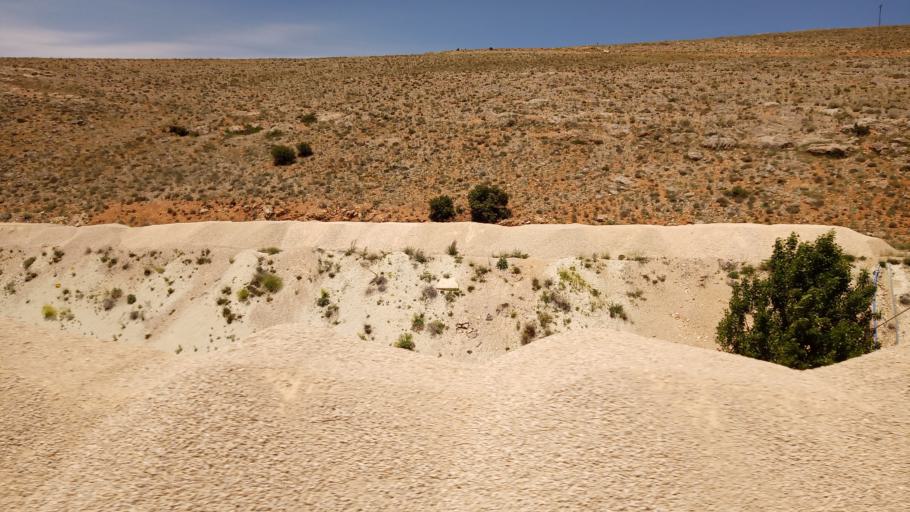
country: TR
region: Malatya
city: Darende
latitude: 38.5864
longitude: 37.4624
